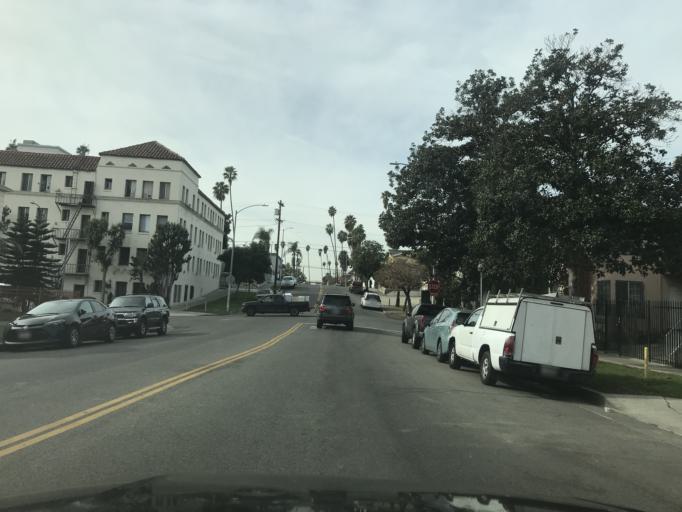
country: US
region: California
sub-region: Los Angeles County
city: Silver Lake
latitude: 34.0728
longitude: -118.2971
